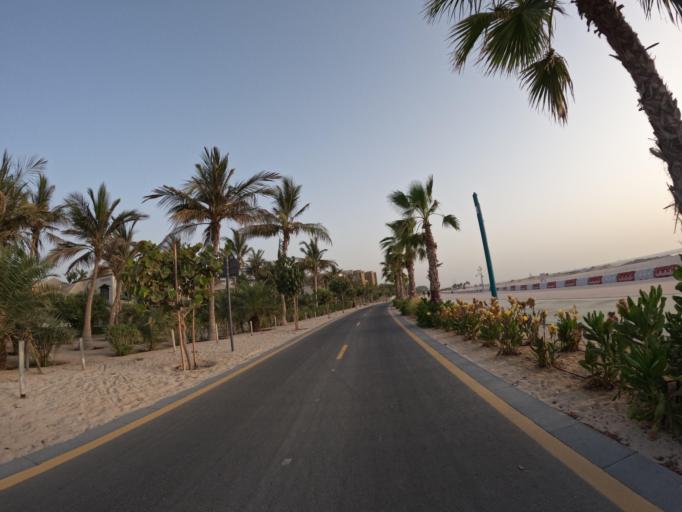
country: AE
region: Dubai
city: Dubai
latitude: 25.1892
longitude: 55.2274
